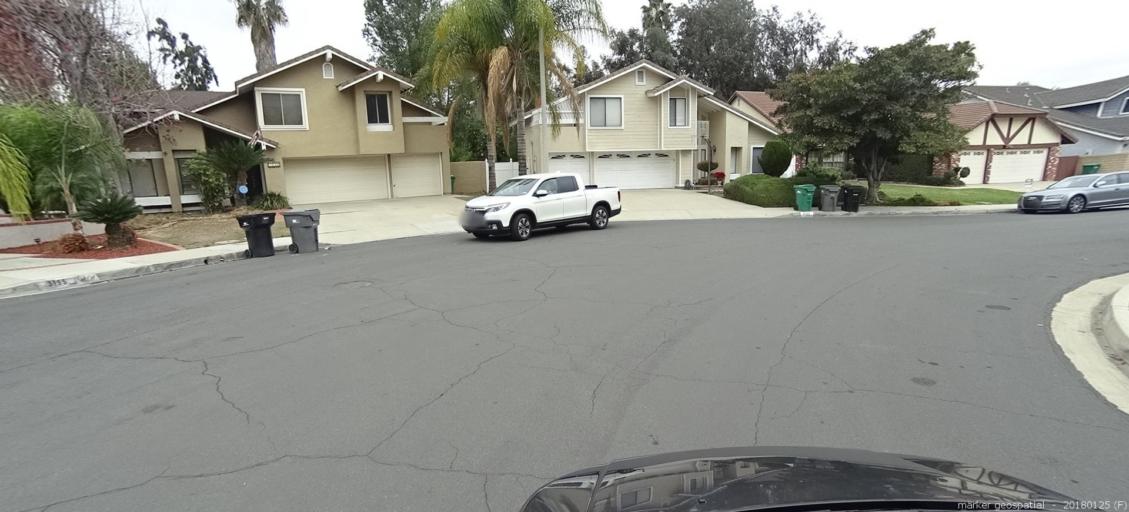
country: US
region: California
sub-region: Los Angeles County
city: Walnut
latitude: 33.9693
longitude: -117.8450
